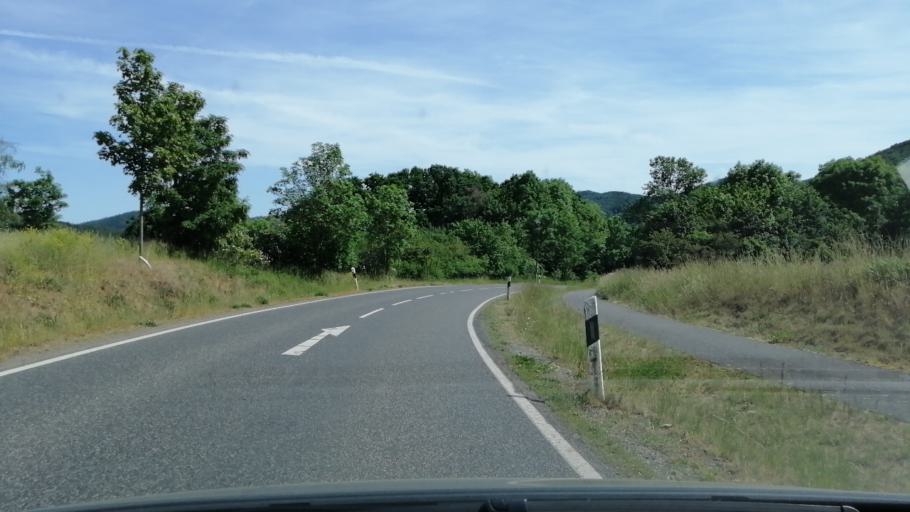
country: DE
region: Hesse
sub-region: Regierungsbezirk Kassel
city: Waldeck
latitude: 51.1773
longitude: 9.0400
